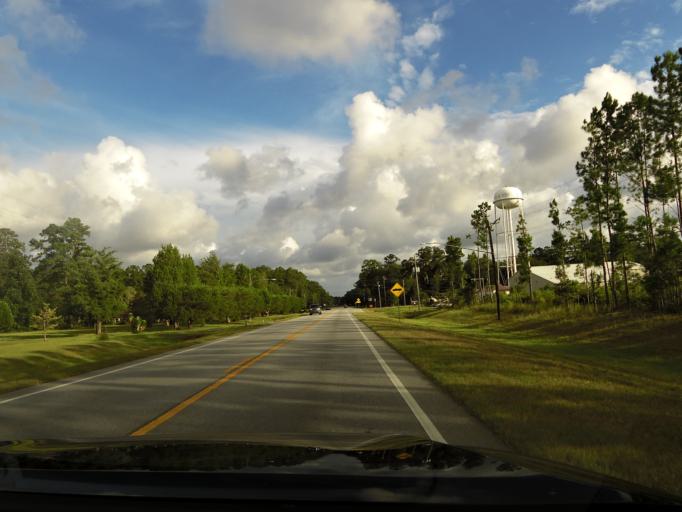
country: US
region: Georgia
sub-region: Liberty County
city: Midway
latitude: 31.7291
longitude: -81.4264
